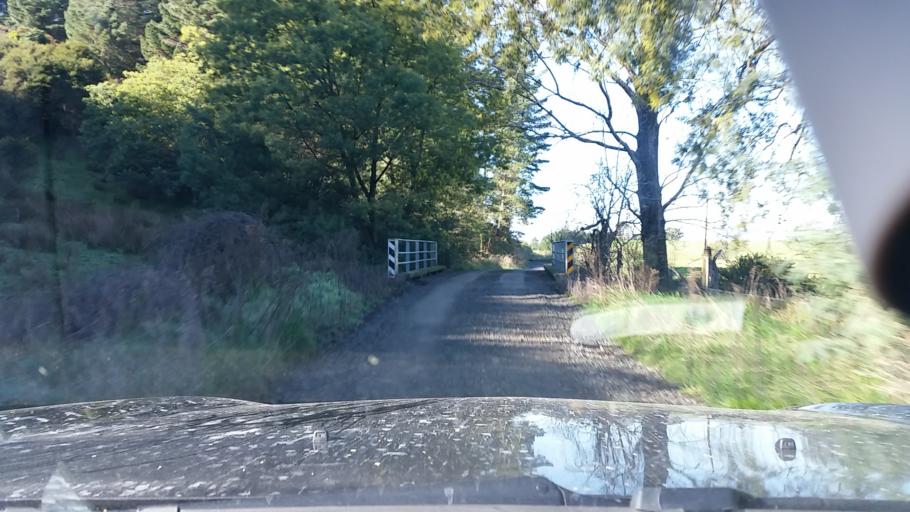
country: NZ
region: Marlborough
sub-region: Marlborough District
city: Blenheim
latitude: -41.4625
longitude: 173.7909
